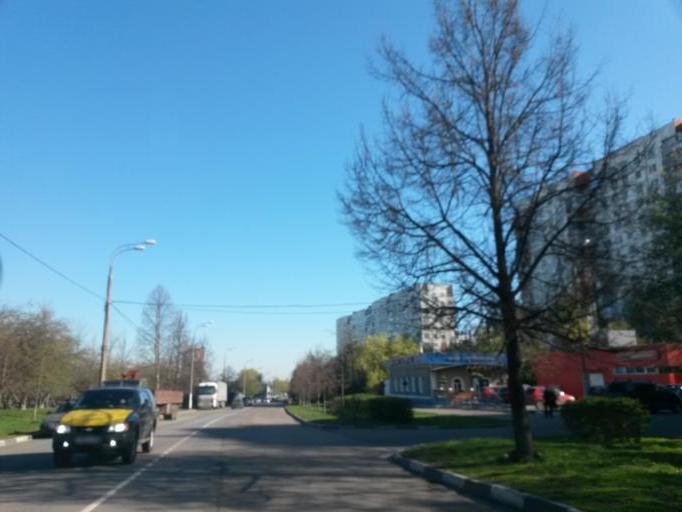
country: RU
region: Moscow
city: Orekhovo-Borisovo
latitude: 55.6183
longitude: 37.7296
